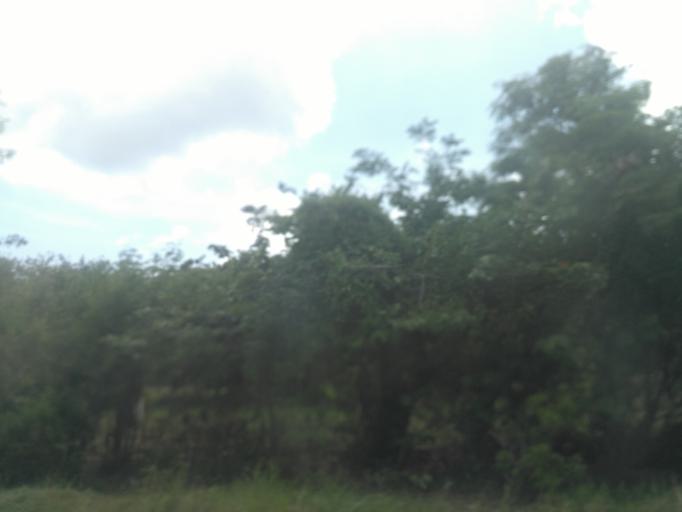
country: TZ
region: Zanzibar Urban/West
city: Zanzibar
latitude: -6.2823
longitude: 39.2798
